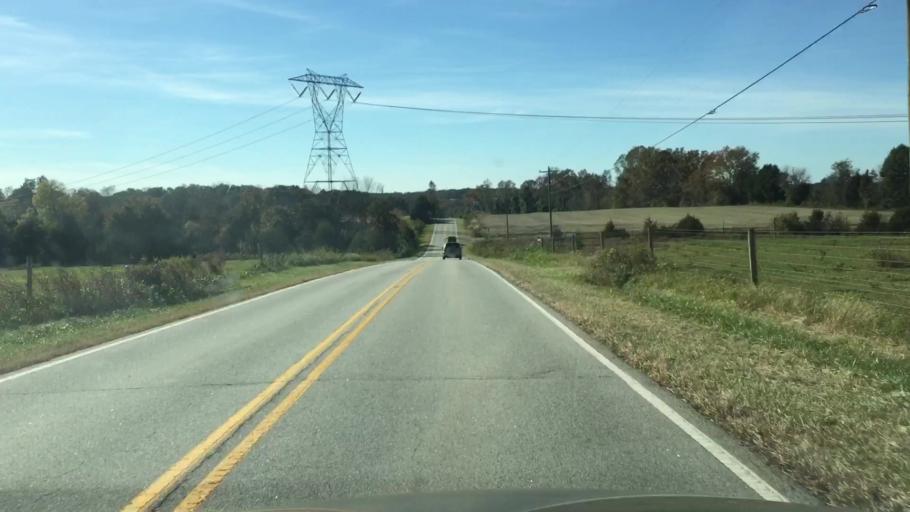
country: US
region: North Carolina
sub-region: Rowan County
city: Enochville
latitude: 35.6233
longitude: -80.6988
